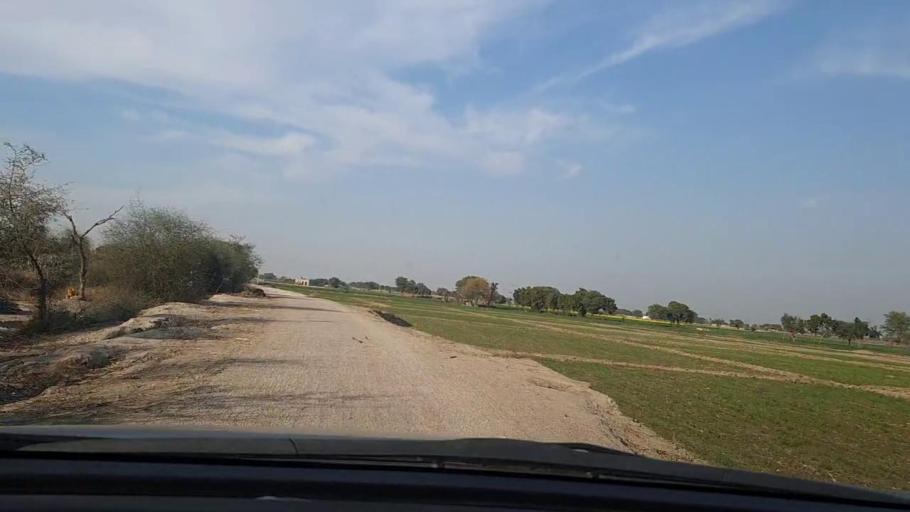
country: PK
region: Sindh
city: Daulatpur
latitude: 26.3244
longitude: 68.0267
